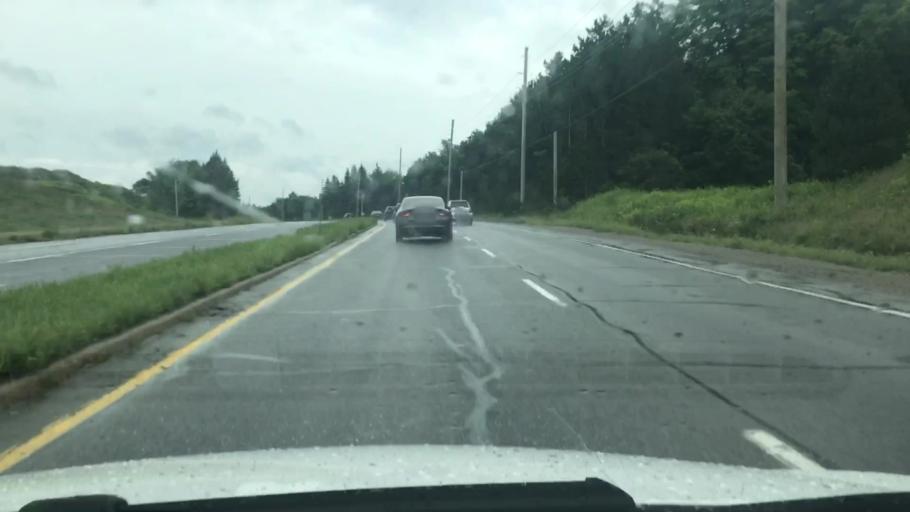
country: CA
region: Ontario
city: Newmarket
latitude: 44.0937
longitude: -79.5090
